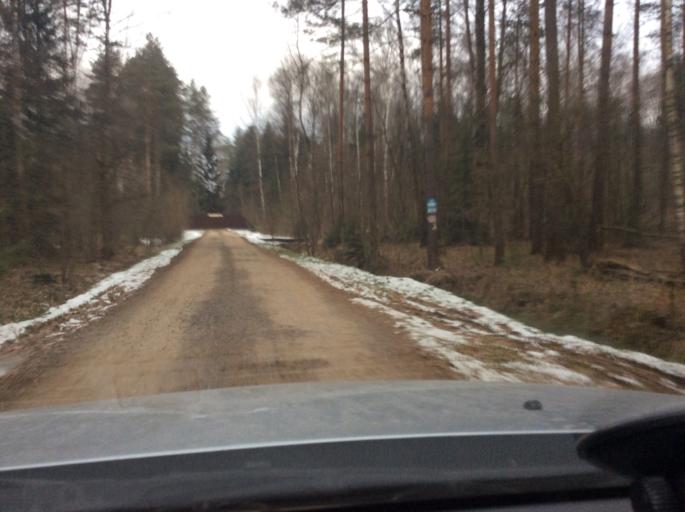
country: RU
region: Moskovskaya
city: Troitsk
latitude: 55.3702
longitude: 37.1642
